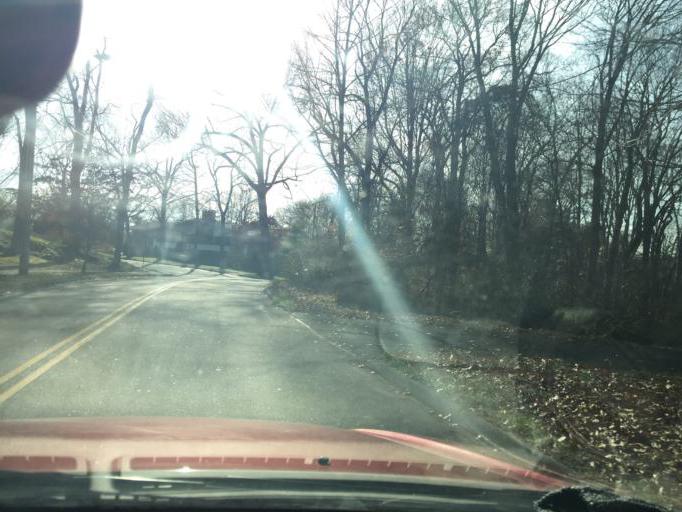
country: US
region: Connecticut
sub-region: Fairfield County
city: Southport
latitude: 41.1421
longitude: -73.2902
